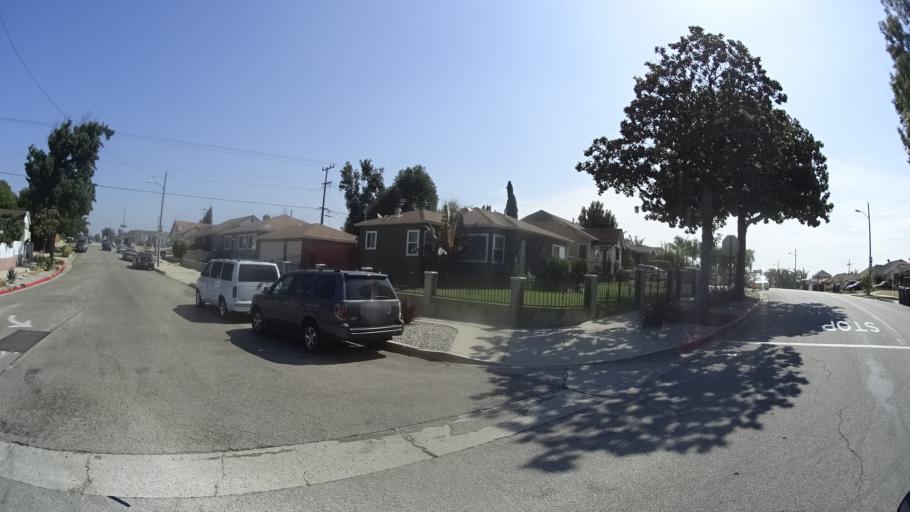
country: US
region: California
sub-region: Los Angeles County
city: View Park-Windsor Hills
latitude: 33.9810
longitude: -118.3439
